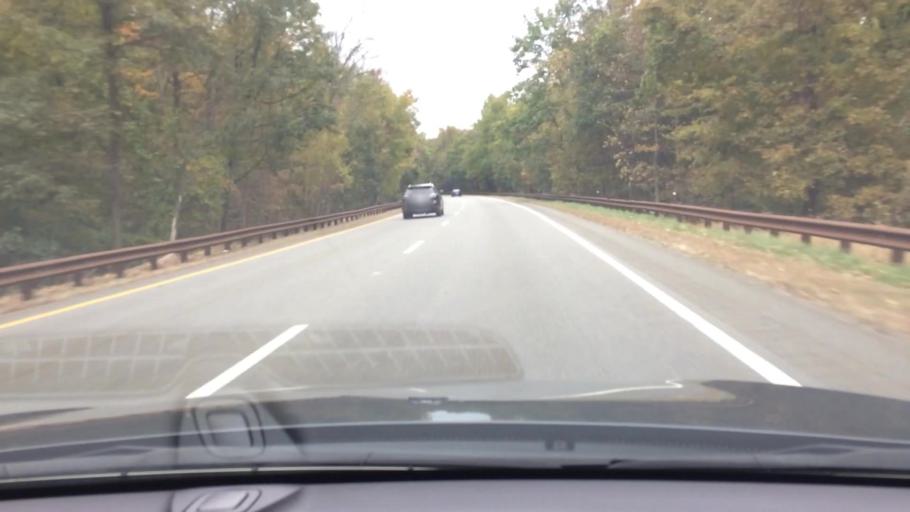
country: US
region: New Jersey
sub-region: Bergen County
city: Alpine
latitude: 40.9670
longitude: -73.9148
